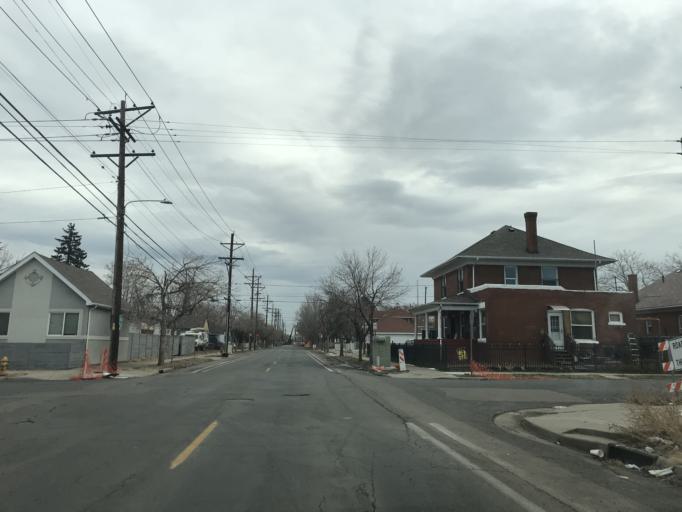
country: US
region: Colorado
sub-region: Adams County
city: Commerce City
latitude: 39.7820
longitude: -104.9636
